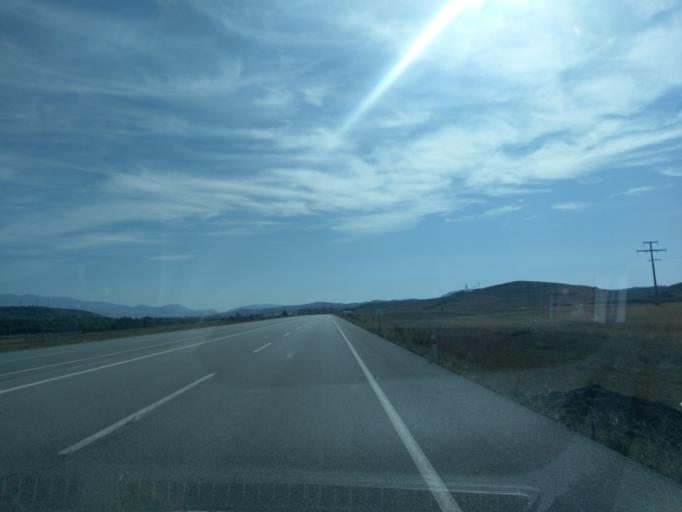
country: TR
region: Sivas
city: Imranli
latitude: 39.8730
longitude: 38.0885
